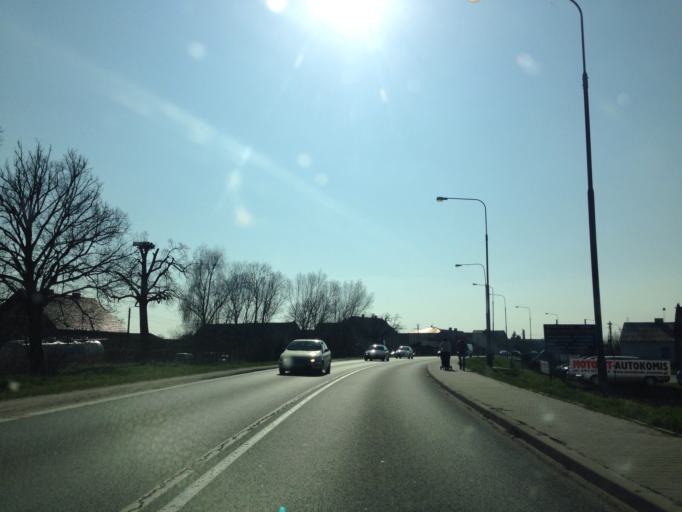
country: PL
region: Lower Silesian Voivodeship
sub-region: Powiat olesnicki
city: Olesnica
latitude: 51.2025
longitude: 17.3304
